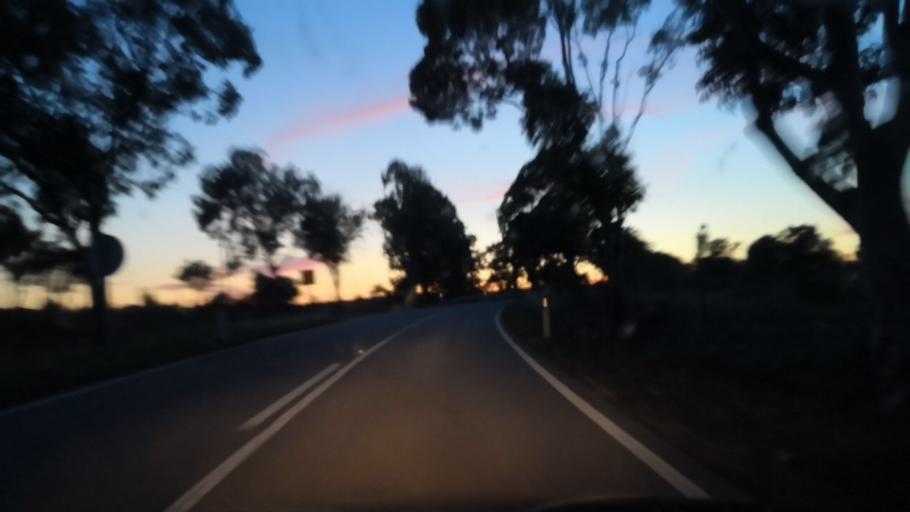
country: ES
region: Extremadura
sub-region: Provincia de Caceres
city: Piedras Albas
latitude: 39.8564
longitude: -6.9950
